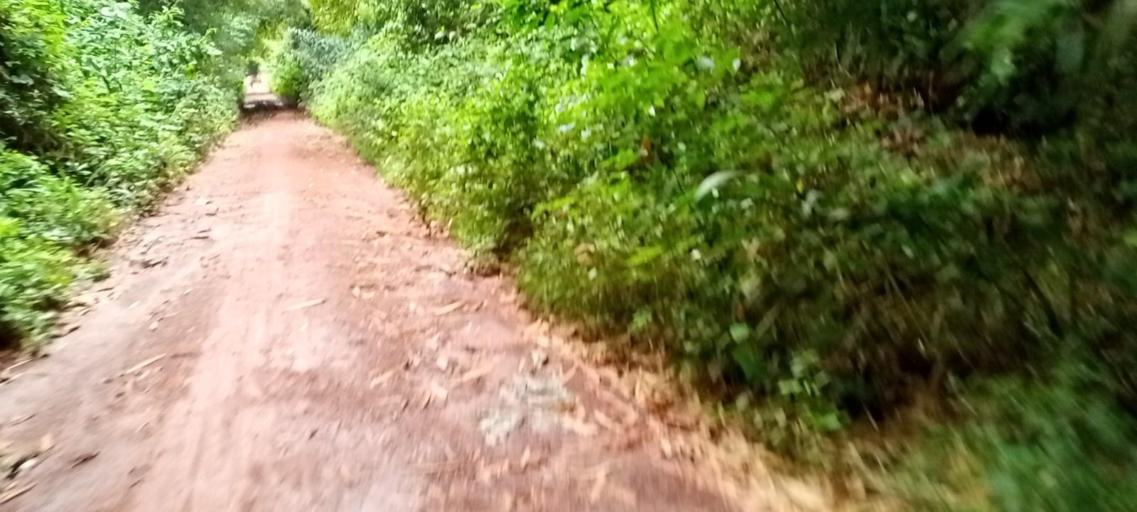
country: CD
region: Eastern Province
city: Aketi
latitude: 2.9179
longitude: 24.0668
